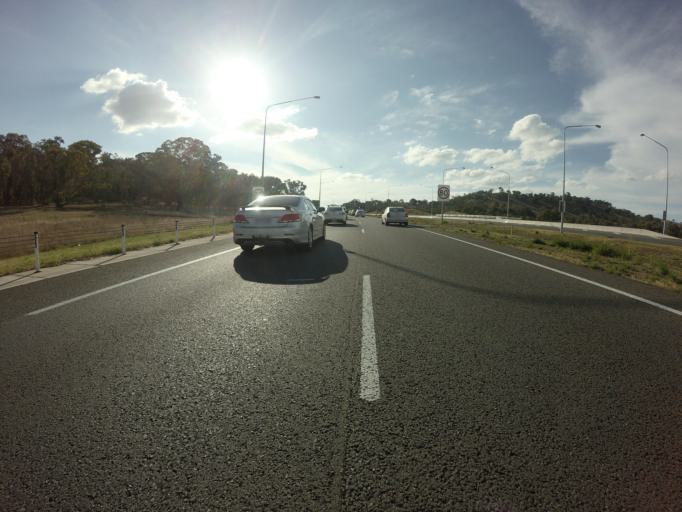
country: AU
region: Australian Capital Territory
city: Kaleen
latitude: -35.2160
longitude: 149.1929
